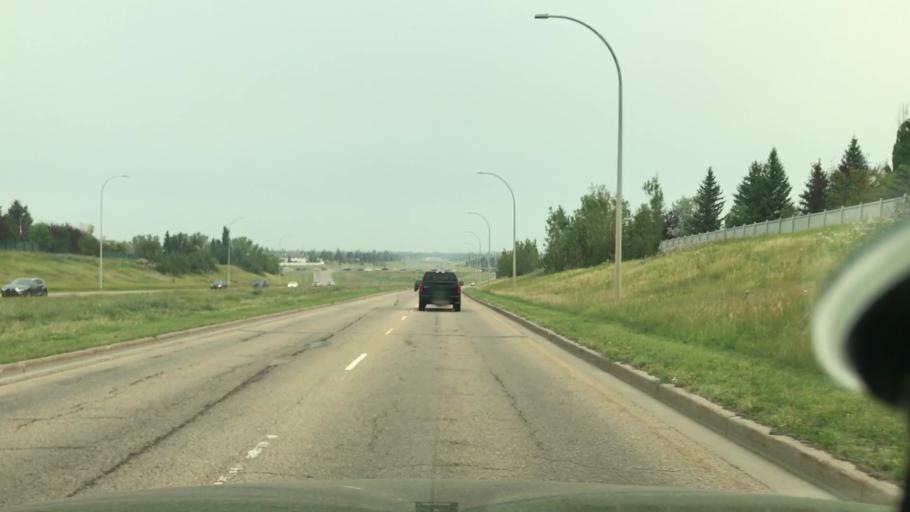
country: CA
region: Alberta
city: Edmonton
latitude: 53.4636
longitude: -113.5854
